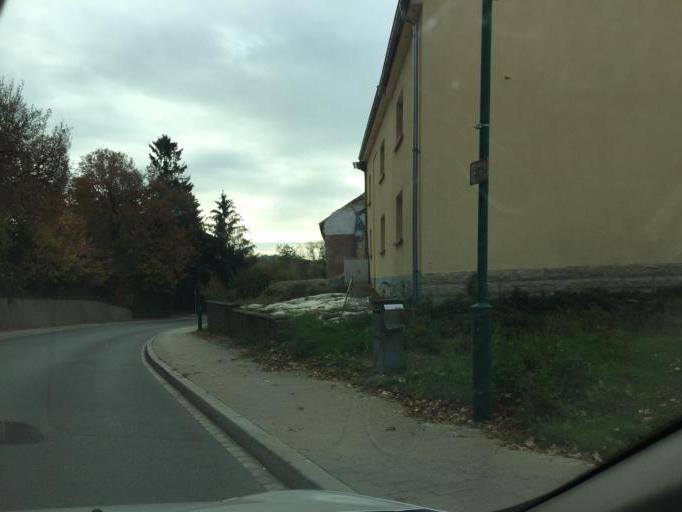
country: LU
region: Luxembourg
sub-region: Canton de Capellen
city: Dippach
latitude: 49.6160
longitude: 5.9877
